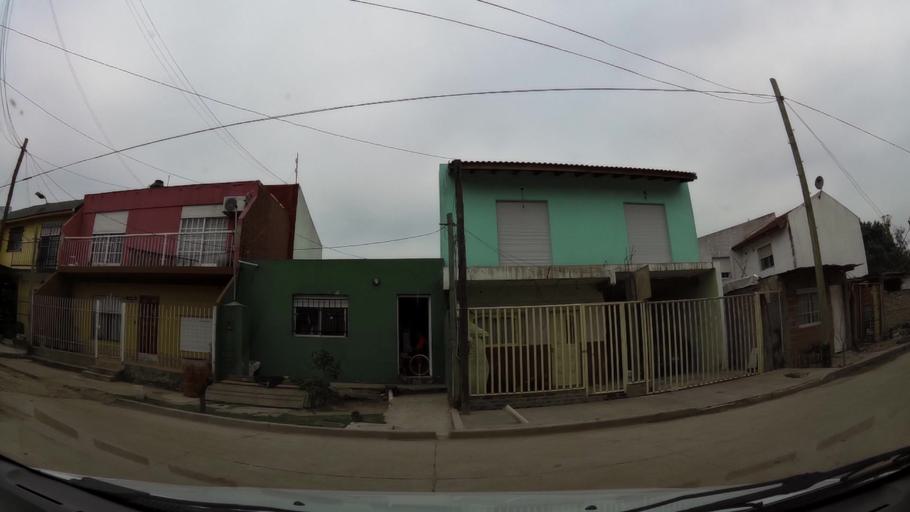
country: AR
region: Buenos Aires
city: San Justo
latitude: -34.6986
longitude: -58.5457
